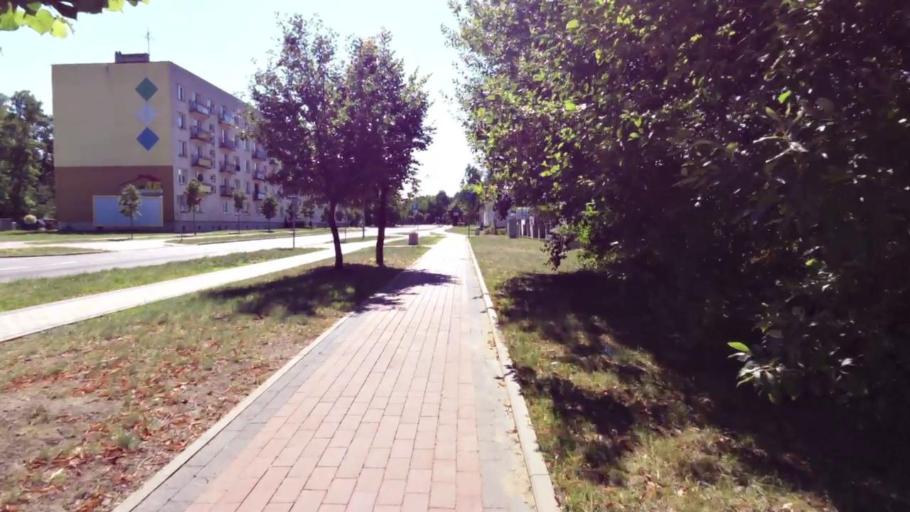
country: PL
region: West Pomeranian Voivodeship
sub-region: Powiat szczecinecki
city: Borne Sulinowo
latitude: 53.5779
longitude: 16.5503
